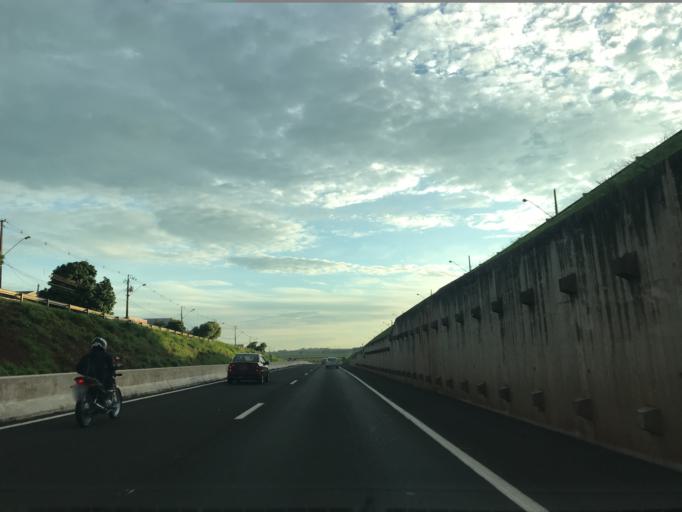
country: BR
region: Parana
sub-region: Maringa
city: Maringa
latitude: -23.3749
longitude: -51.9362
